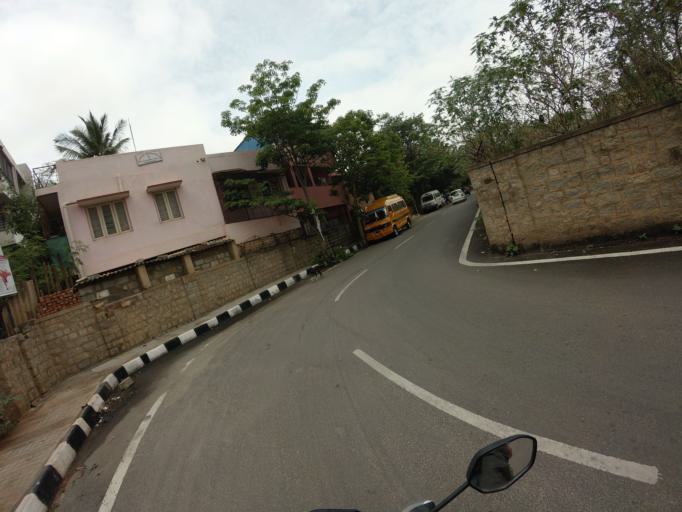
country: IN
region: Karnataka
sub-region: Bangalore Urban
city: Bangalore
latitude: 12.9710
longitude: 77.6689
